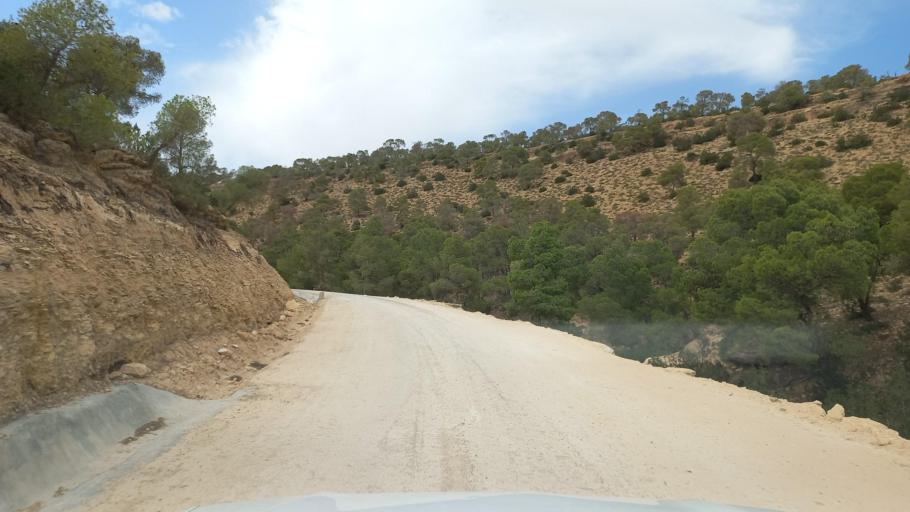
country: TN
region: Al Qasrayn
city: Kasserine
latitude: 35.3765
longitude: 8.8868
